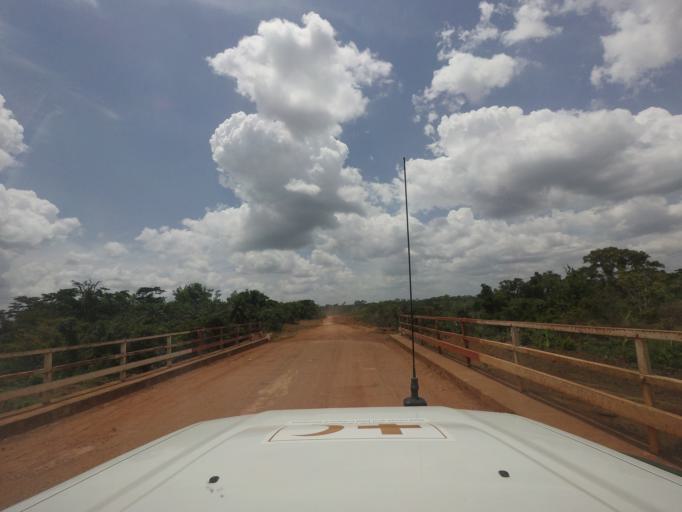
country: LR
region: Nimba
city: Sanniquellie
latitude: 7.2310
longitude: -8.9002
